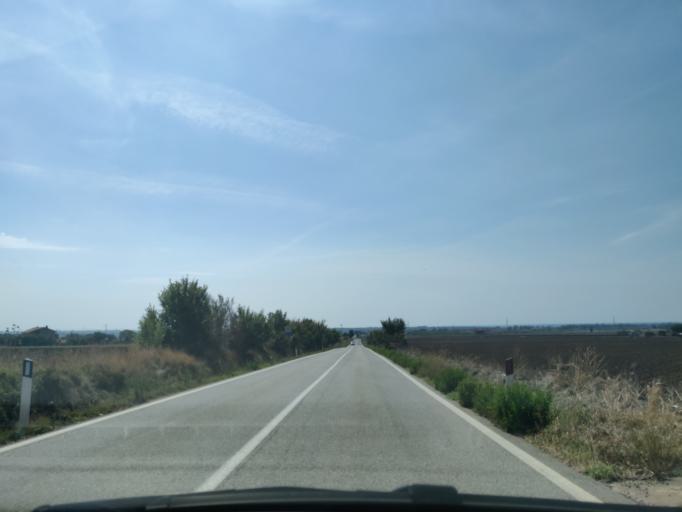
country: IT
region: Latium
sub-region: Provincia di Viterbo
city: Tarquinia
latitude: 42.2191
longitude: 11.7846
